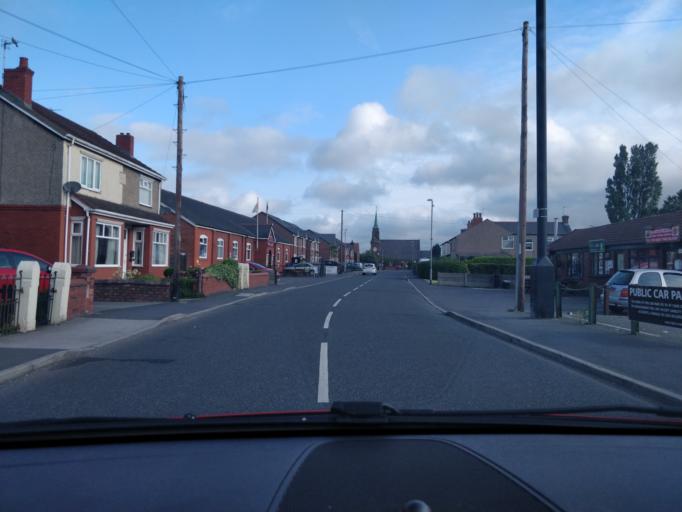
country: GB
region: England
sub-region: Lancashire
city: Banks
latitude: 53.6796
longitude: -2.9240
